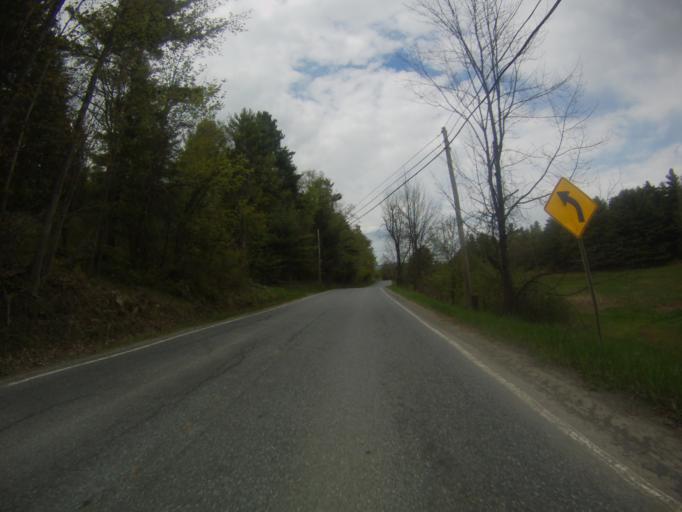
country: US
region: New York
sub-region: Essex County
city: Port Henry
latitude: 43.9875
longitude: -73.4909
